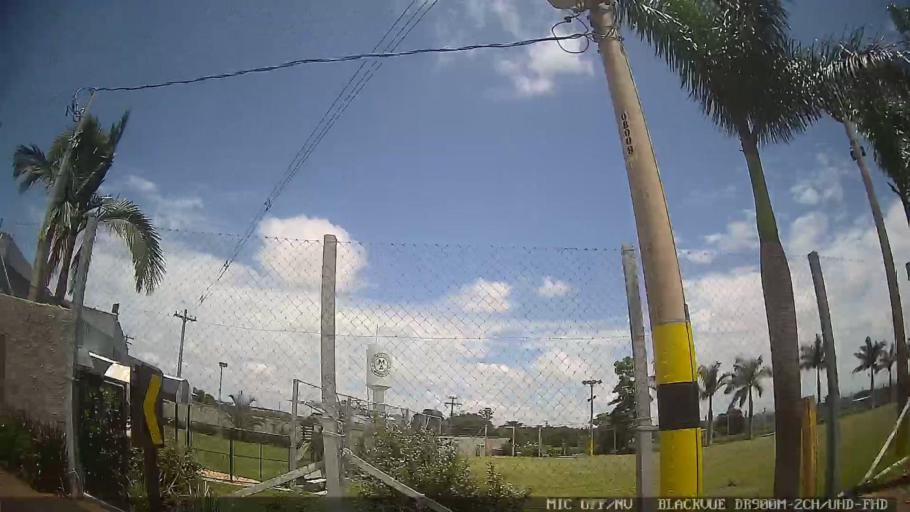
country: BR
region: Sao Paulo
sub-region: Laranjal Paulista
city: Laranjal Paulista
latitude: -23.0324
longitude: -47.8587
